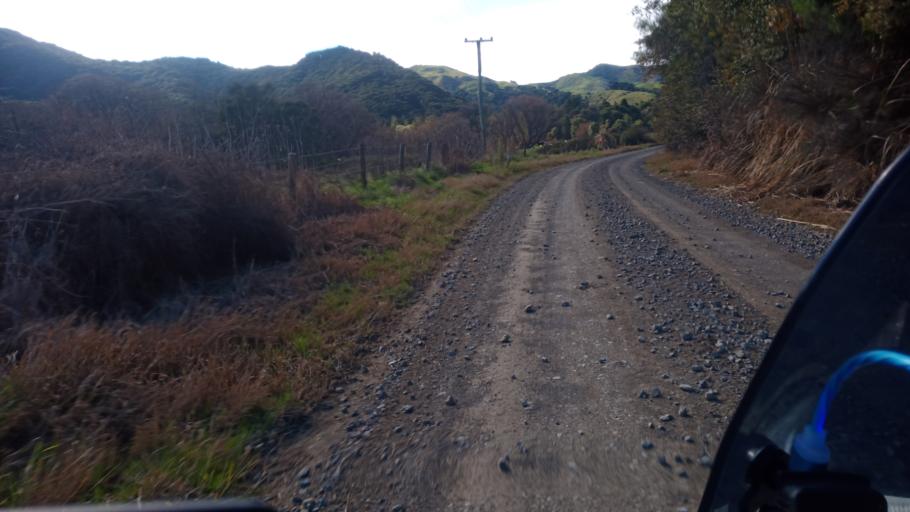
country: NZ
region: Gisborne
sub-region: Gisborne District
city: Gisborne
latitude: -38.2937
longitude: 178.2784
